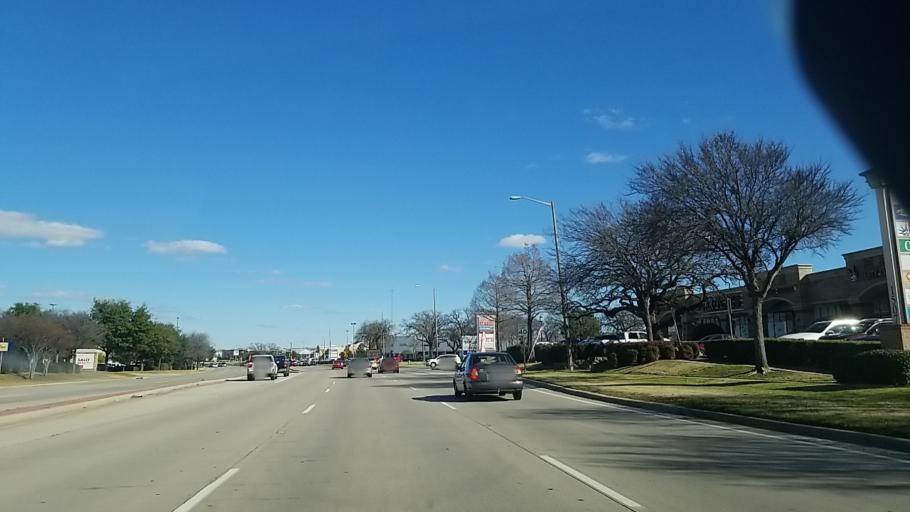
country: US
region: Texas
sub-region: Denton County
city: Denton
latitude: 33.1935
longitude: -97.0950
